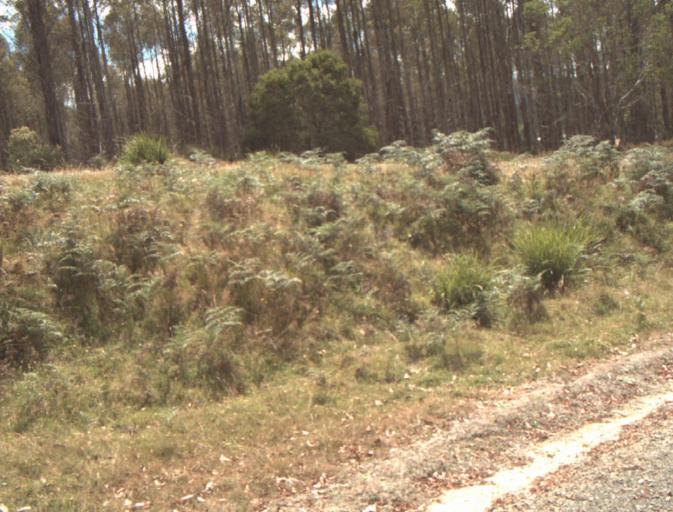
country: AU
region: Tasmania
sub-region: Dorset
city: Scottsdale
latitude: -41.4180
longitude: 147.5221
